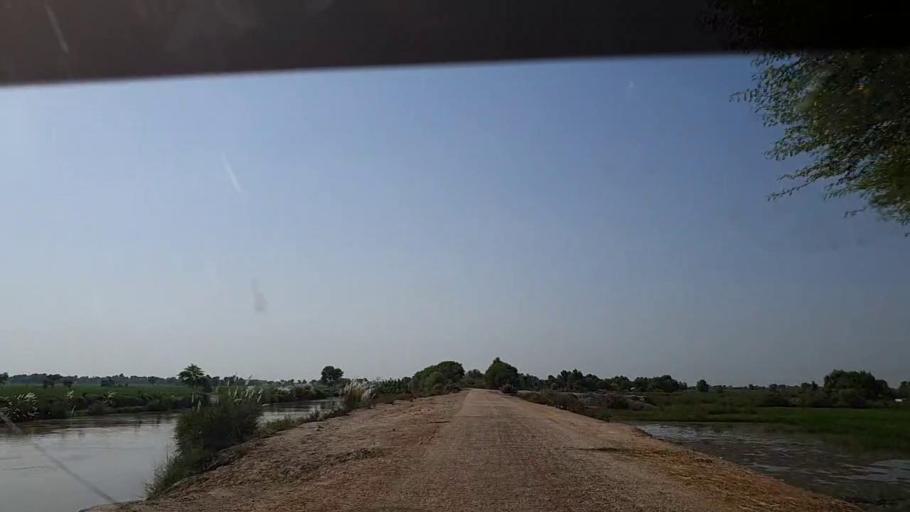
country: PK
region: Sindh
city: Ghauspur
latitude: 28.1874
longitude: 69.0650
